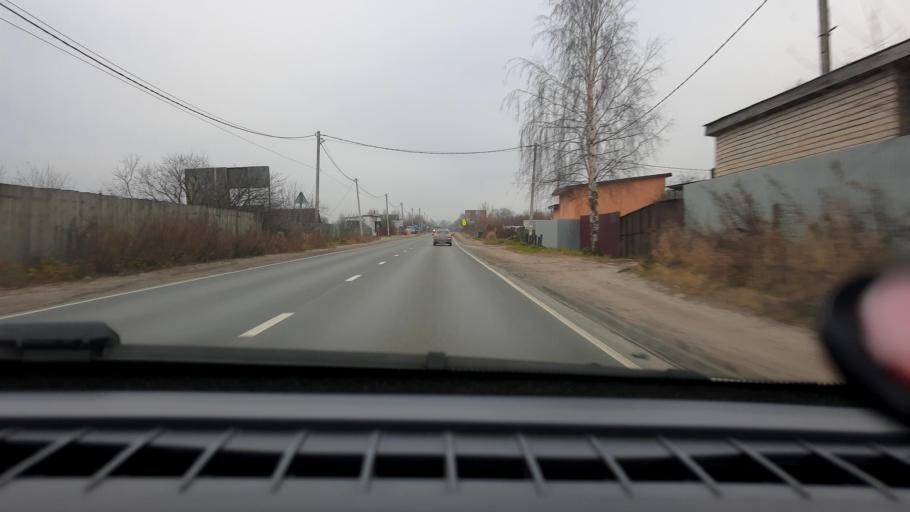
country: RU
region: Nizjnij Novgorod
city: Gidrotorf
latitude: 56.5462
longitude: 43.5262
